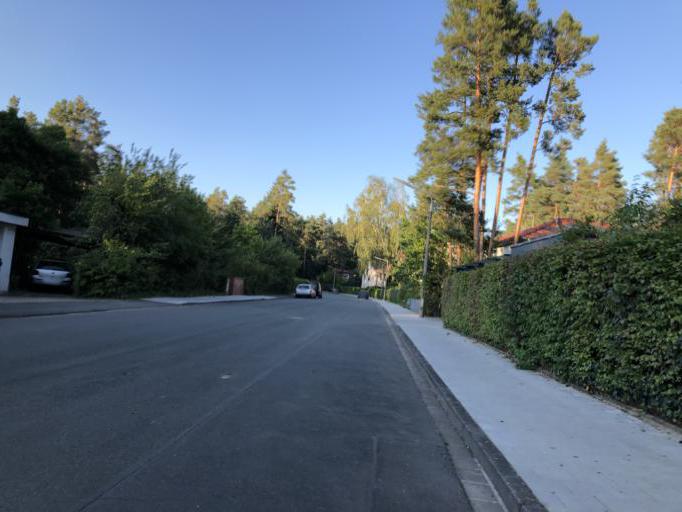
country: DE
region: Bavaria
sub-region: Regierungsbezirk Mittelfranken
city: Buckenhof
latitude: 49.6032
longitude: 11.0307
